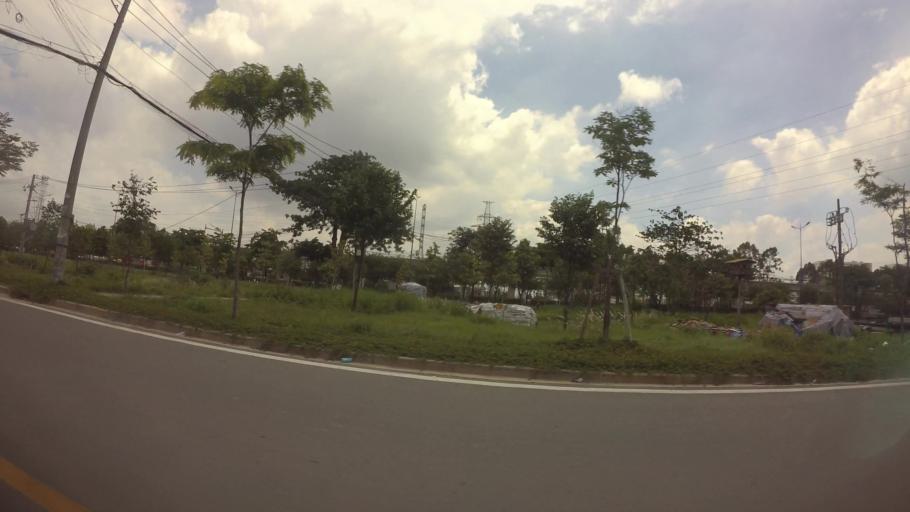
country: VN
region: Ho Chi Minh City
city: Quan Chin
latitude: 10.8323
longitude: 106.7649
